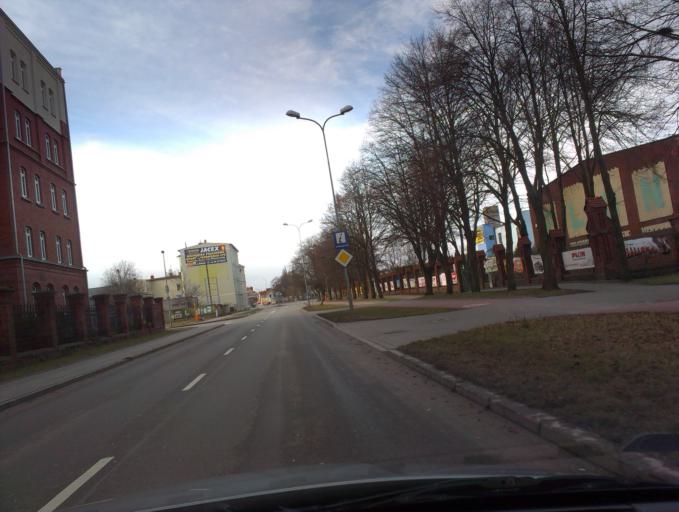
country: PL
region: West Pomeranian Voivodeship
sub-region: Powiat kolobrzeski
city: Kolobrzeg
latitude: 54.1726
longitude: 15.5607
